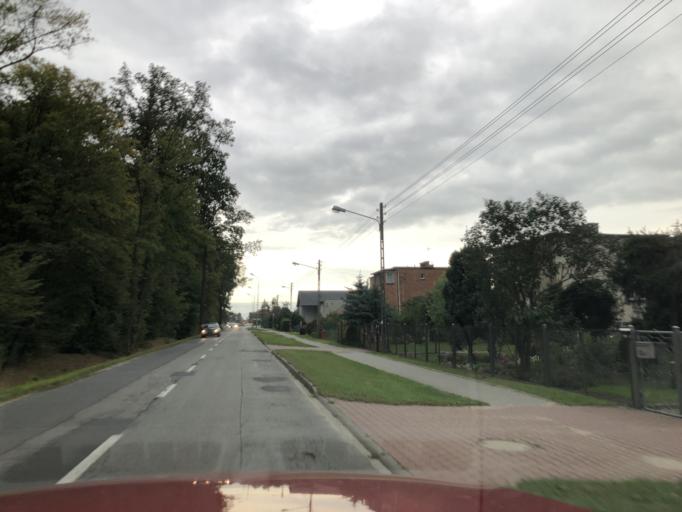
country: PL
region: Lower Silesian Voivodeship
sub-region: Powiat wroclawski
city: Dlugoleka
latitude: 51.1810
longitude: 17.1897
